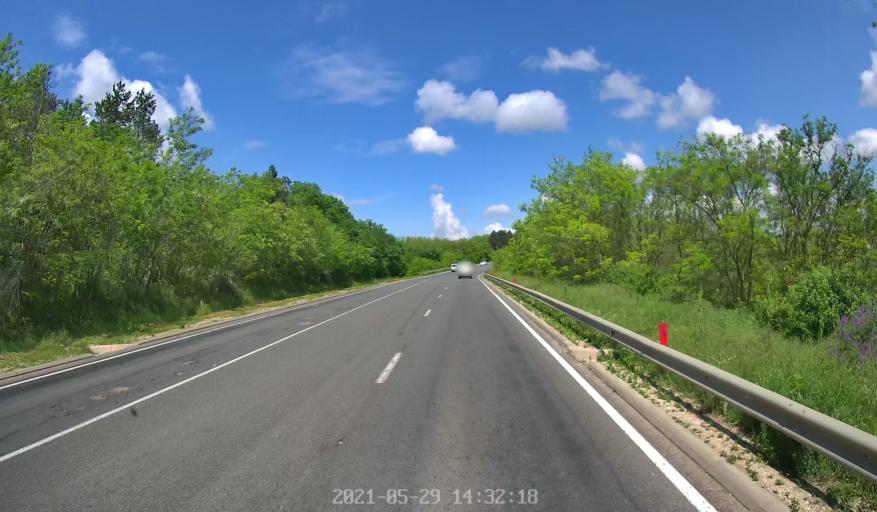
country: MD
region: Hincesti
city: Hincesti
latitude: 46.8774
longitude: 28.6509
